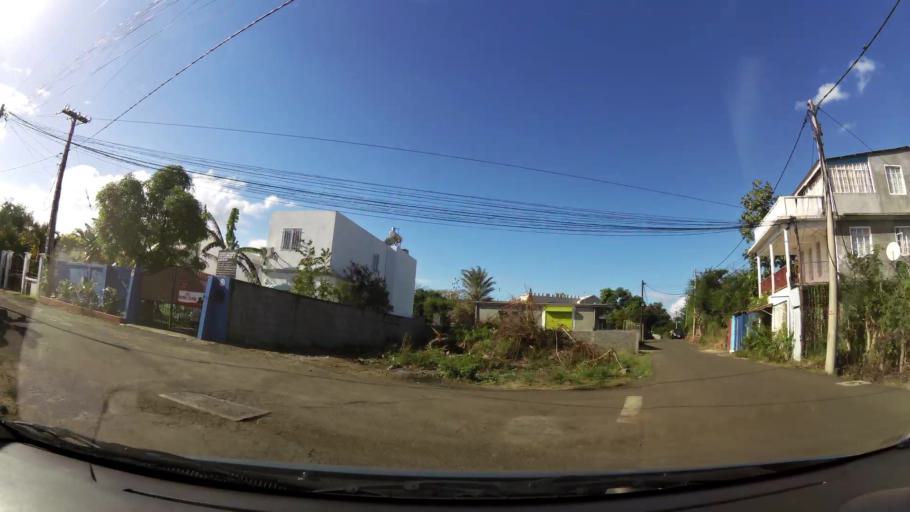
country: MU
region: Black River
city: Albion
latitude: -20.2063
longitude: 57.4135
